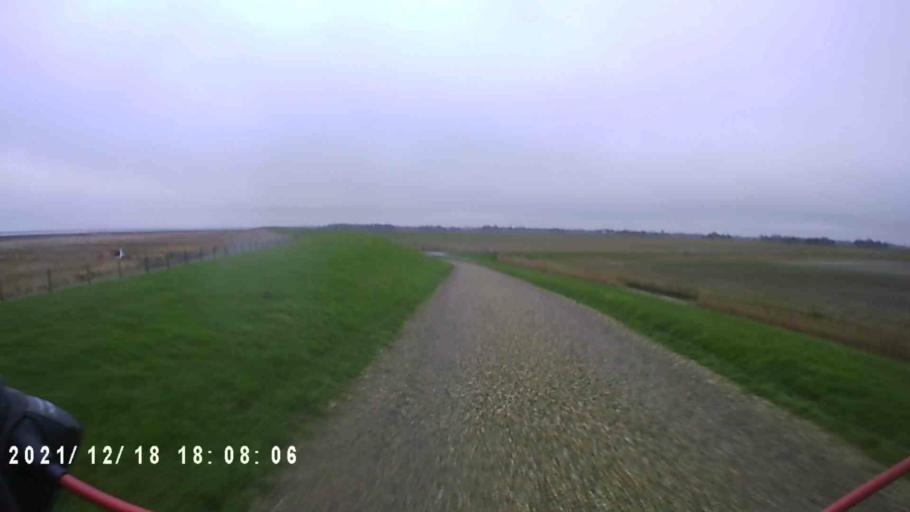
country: NL
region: Friesland
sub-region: Gemeente Dongeradeel
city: Holwerd
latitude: 53.3852
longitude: 5.9218
